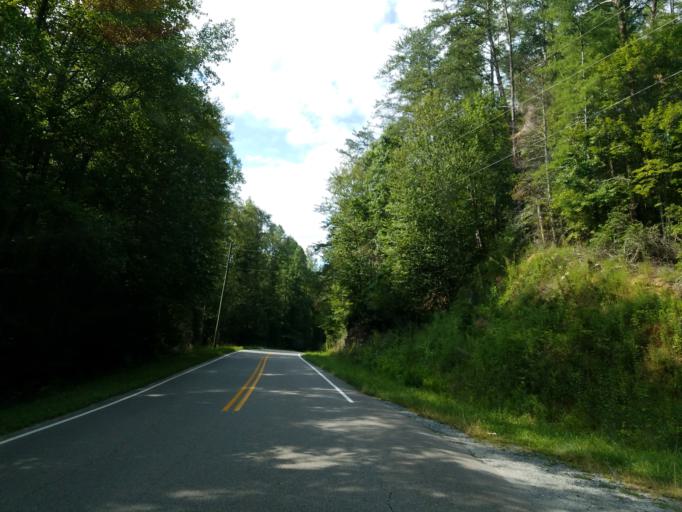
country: US
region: Georgia
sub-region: Gilmer County
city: Ellijay
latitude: 34.7496
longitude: -84.4206
